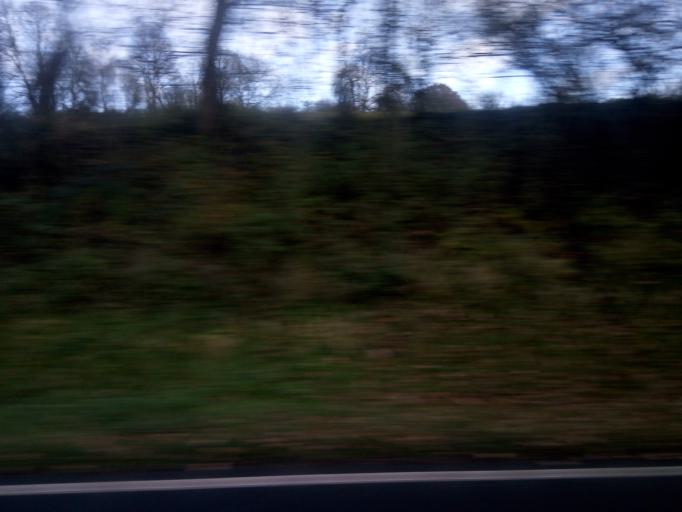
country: LU
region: Diekirch
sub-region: Canton de Vianden
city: Tandel
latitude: 49.9087
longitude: 6.1912
